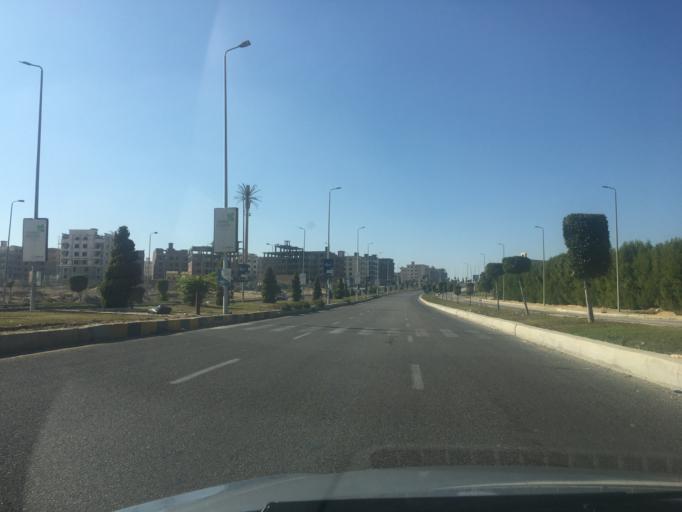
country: EG
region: Al Jizah
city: Awsim
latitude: 30.0196
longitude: 30.9891
